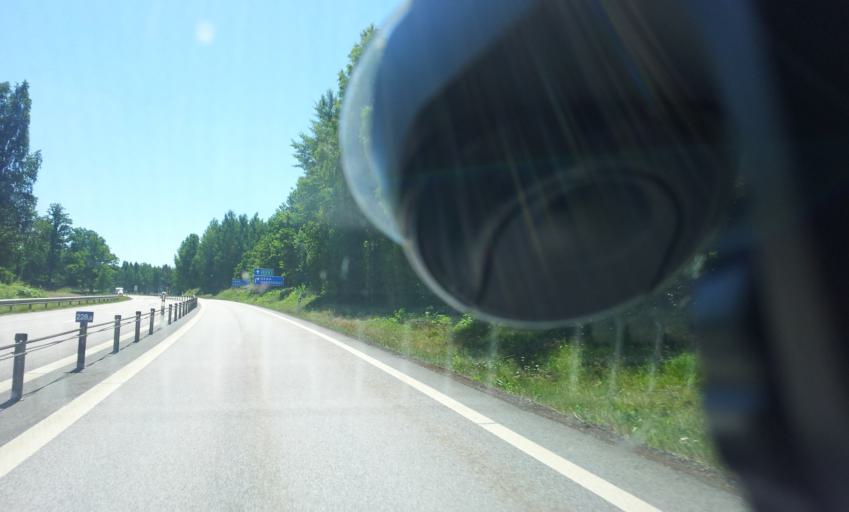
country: SE
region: Kalmar
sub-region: Vasterviks Kommun
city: Forserum
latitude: 58.0775
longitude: 16.5177
